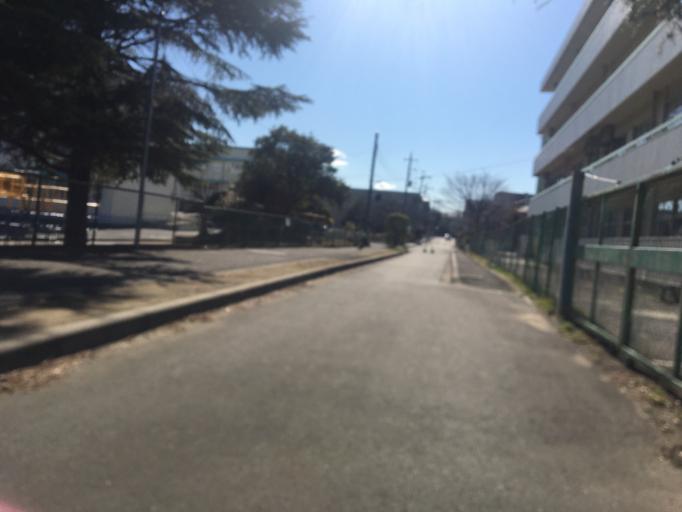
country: JP
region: Saitama
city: Shiki
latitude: 35.8271
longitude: 139.5625
